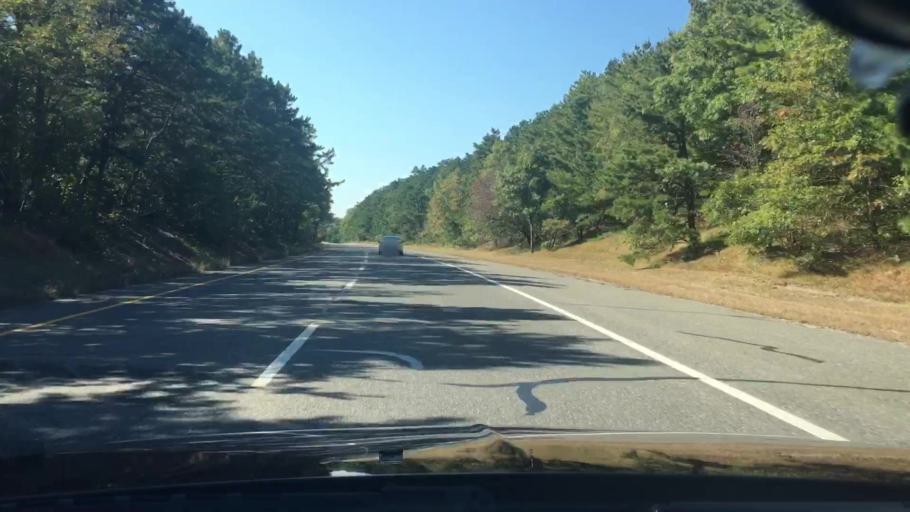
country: US
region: New York
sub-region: Suffolk County
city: North Patchogue
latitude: 40.7950
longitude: -73.0312
